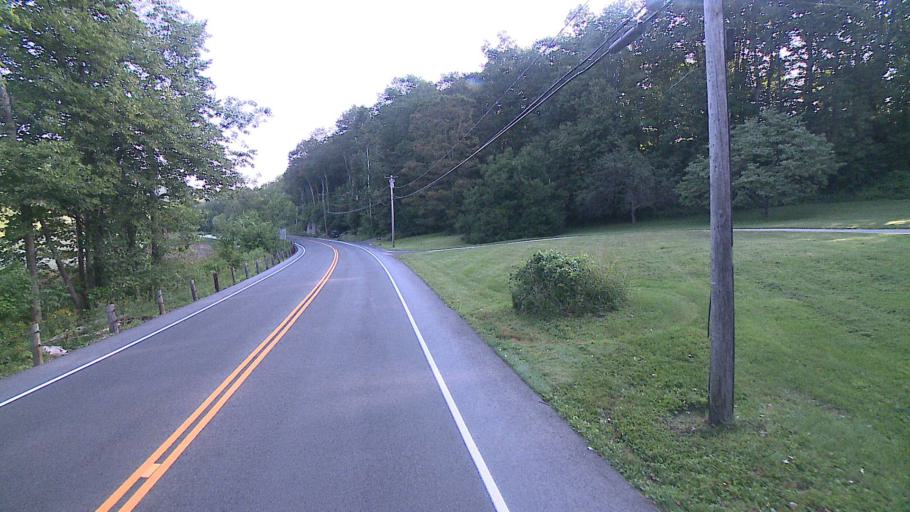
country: US
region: Connecticut
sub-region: Litchfield County
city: Kent
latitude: 41.6781
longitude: -73.5074
